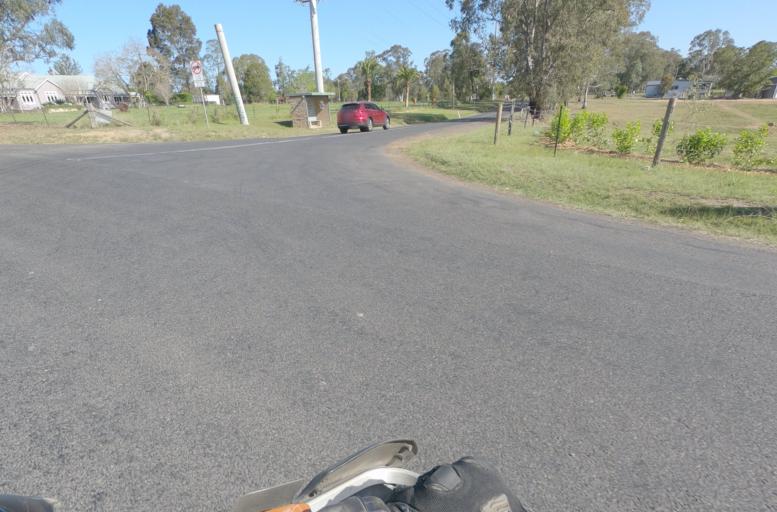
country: AU
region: New South Wales
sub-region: Hawkesbury
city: Scheyville
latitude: -33.5633
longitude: 150.9132
